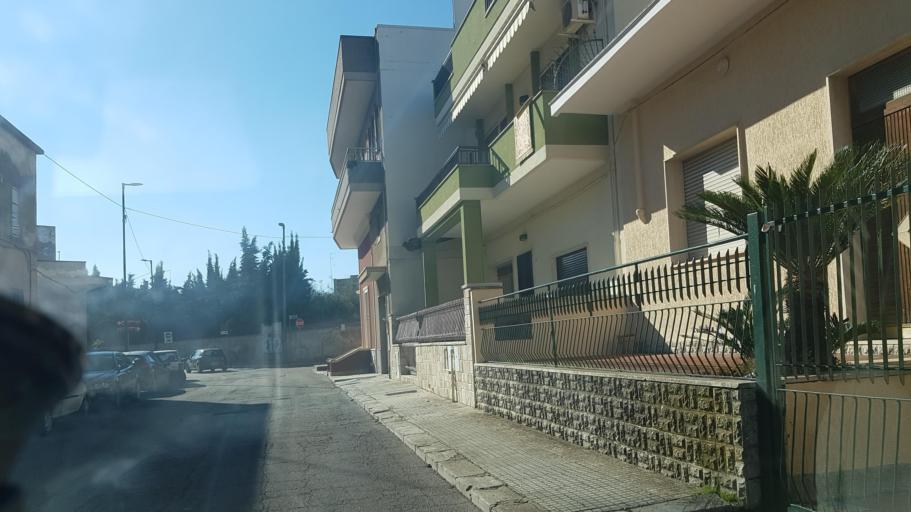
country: IT
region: Apulia
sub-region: Provincia di Lecce
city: Arnesano
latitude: 40.3388
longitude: 18.0893
